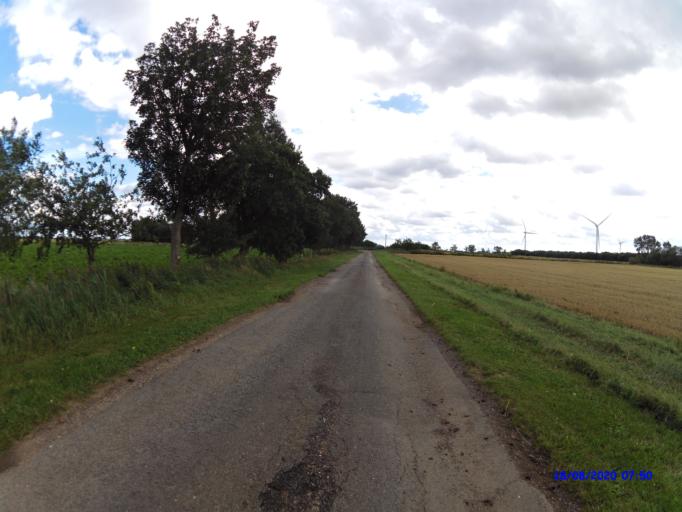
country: GB
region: England
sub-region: Cambridgeshire
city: Whittlesey
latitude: 52.5196
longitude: -0.0935
